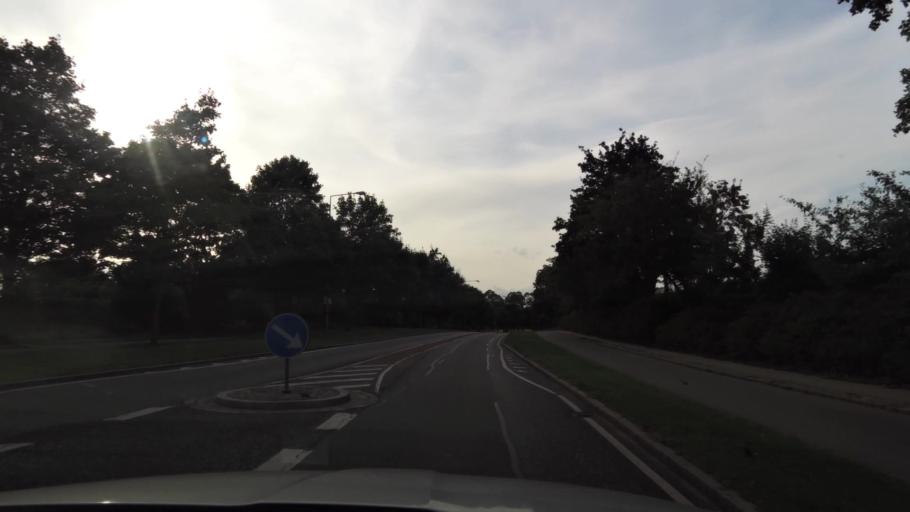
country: DK
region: Capital Region
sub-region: Rudersdal Kommune
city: Birkerod
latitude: 55.8327
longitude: 12.4214
